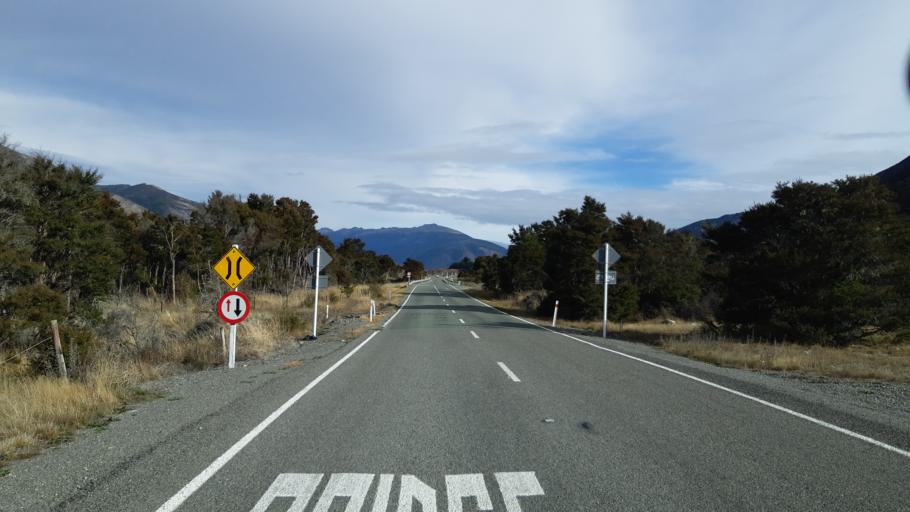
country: NZ
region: Tasman
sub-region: Tasman District
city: Wakefield
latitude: -41.7297
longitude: 173.0354
